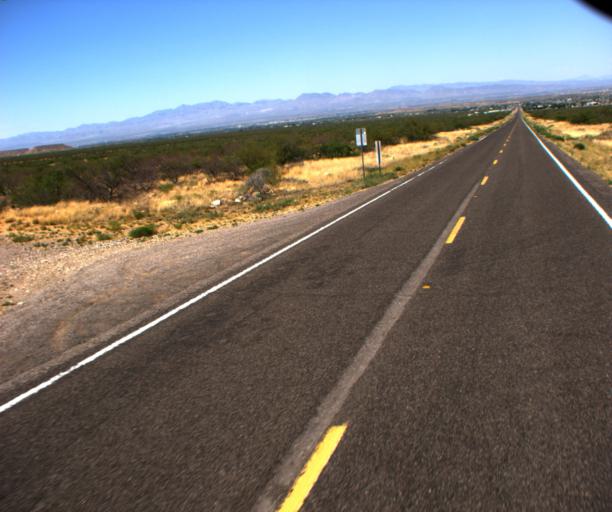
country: US
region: Arizona
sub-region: Graham County
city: Swift Trail Junction
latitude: 32.7038
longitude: -109.7405
